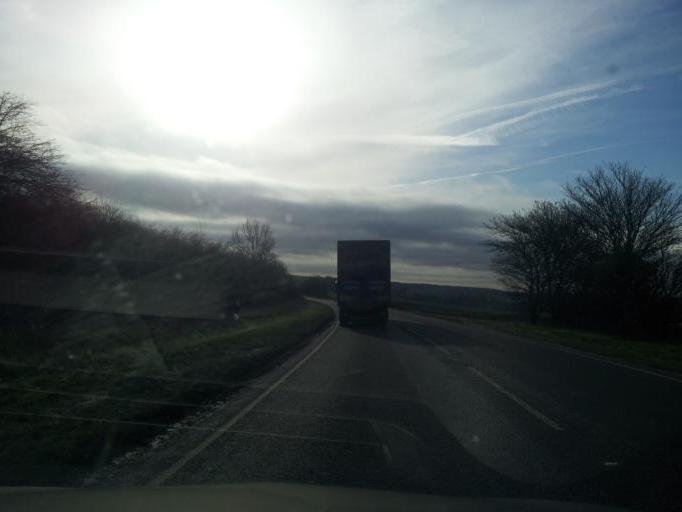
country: GB
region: England
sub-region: District of Rutland
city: Ketton
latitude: 52.6069
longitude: -0.5358
